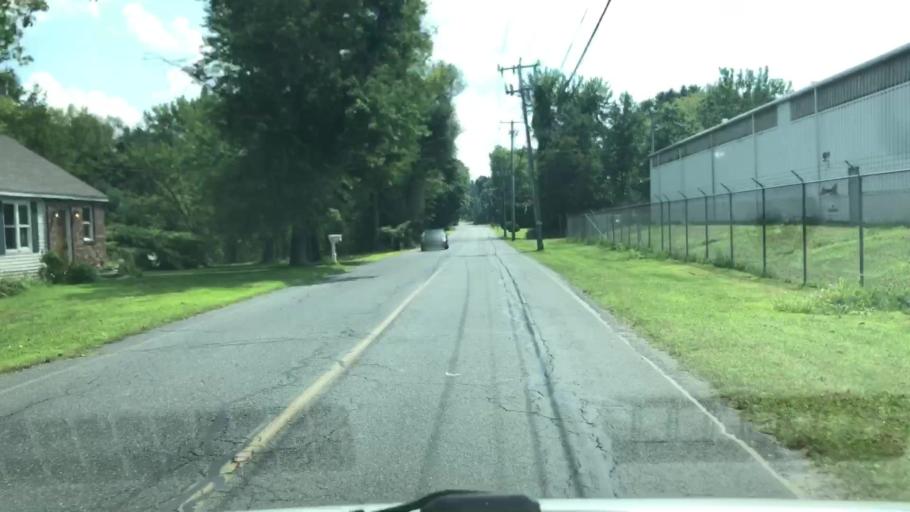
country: US
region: Massachusetts
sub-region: Hampshire County
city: Hatfield
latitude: 42.3655
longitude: -72.6304
